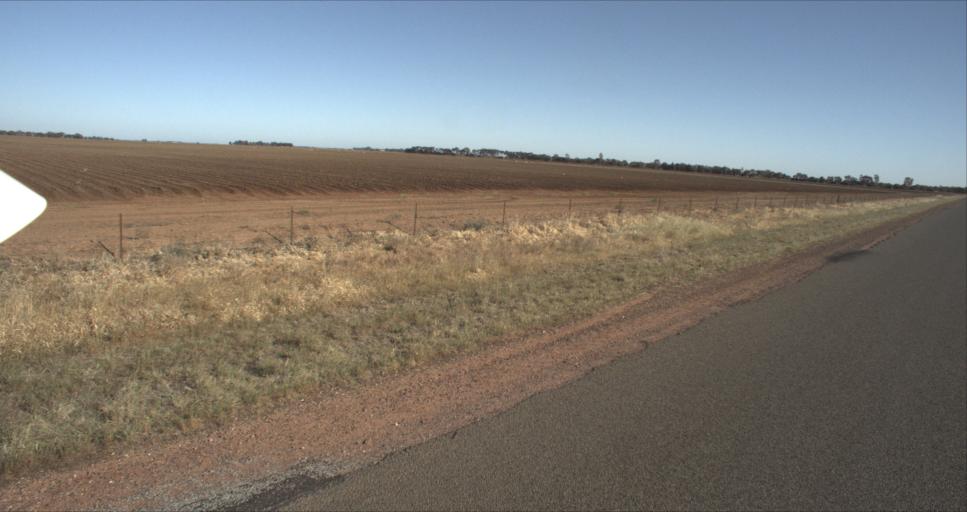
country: AU
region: New South Wales
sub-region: Leeton
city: Leeton
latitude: -34.5751
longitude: 146.2627
